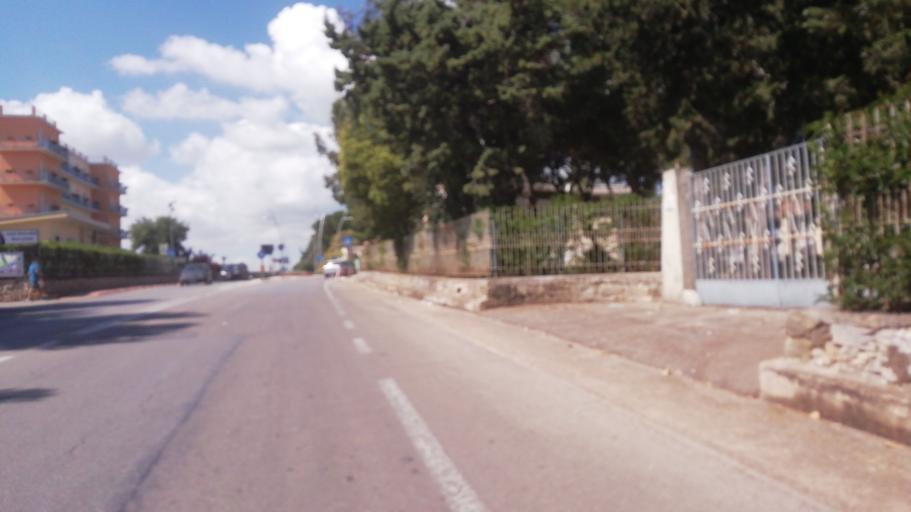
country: IT
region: Apulia
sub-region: Provincia di Bari
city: Corato
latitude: 41.1286
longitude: 16.3829
